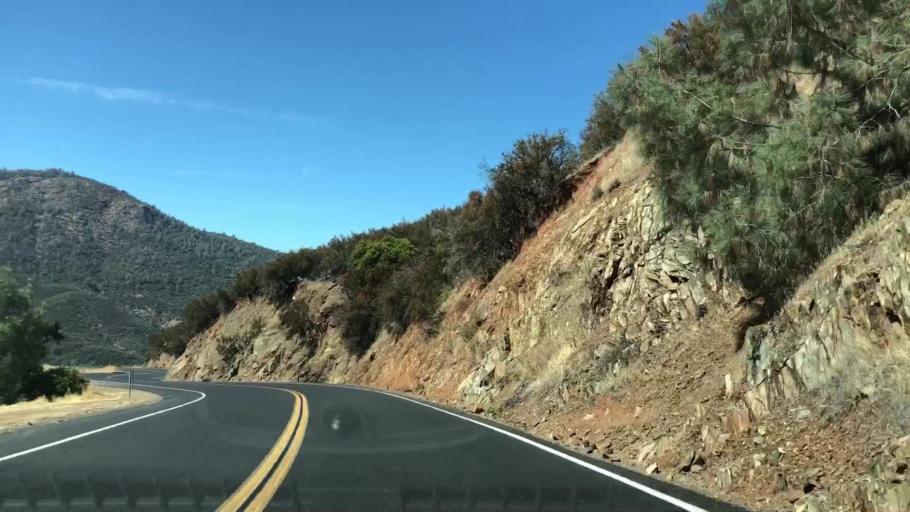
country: US
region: California
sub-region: Tuolumne County
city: Tuolumne City
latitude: 37.8207
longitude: -120.2993
